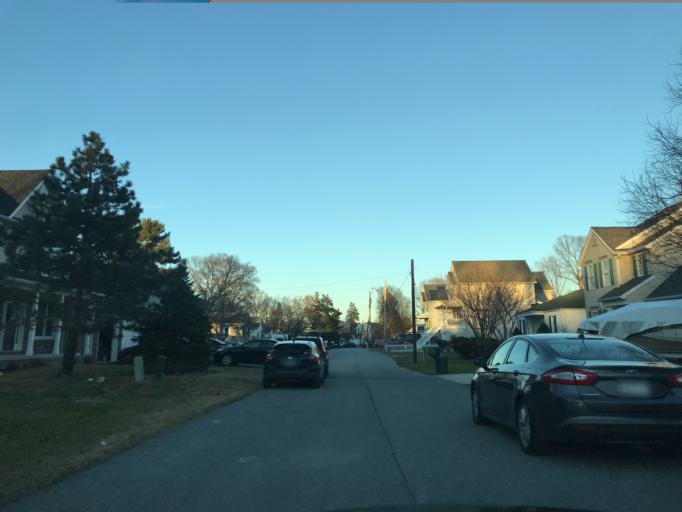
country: US
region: Maryland
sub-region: Baltimore County
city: Bowleys Quarters
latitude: 39.3755
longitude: -76.3545
